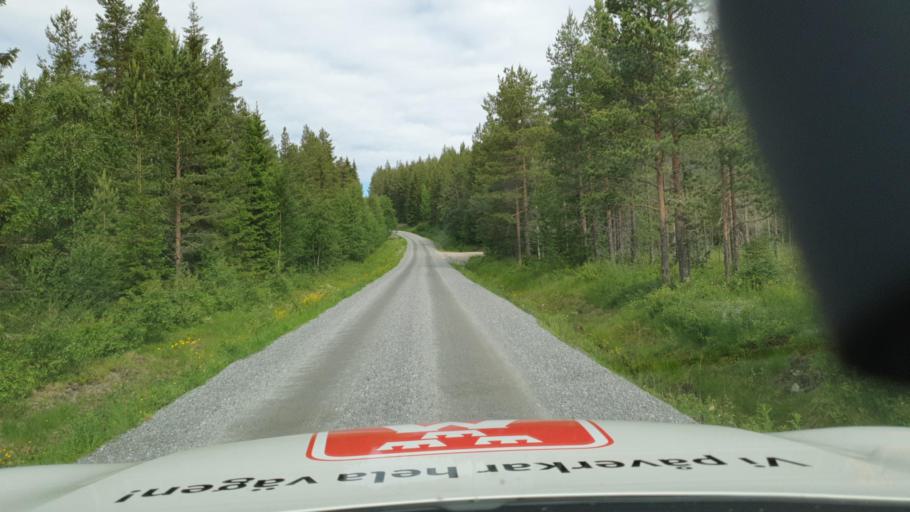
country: SE
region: Vaesterbotten
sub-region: Skelleftea Kommun
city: Langsele
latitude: 64.5868
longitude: 20.2983
